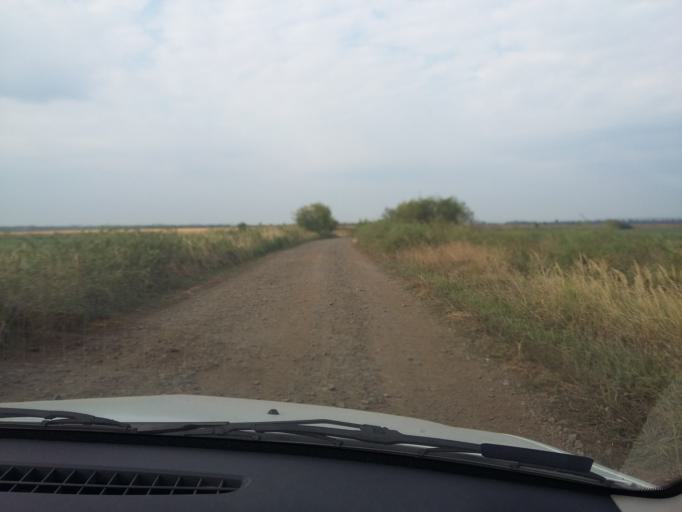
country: HU
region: Borsod-Abauj-Zemplen
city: Taktaharkany
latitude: 48.1365
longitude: 21.1123
